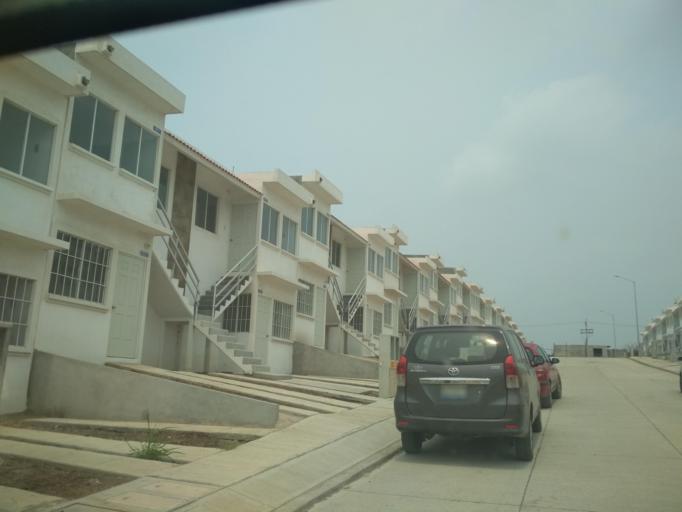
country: MX
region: Veracruz
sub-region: Veracruz
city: Rio Medio [Granja]
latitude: 19.2104
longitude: -96.2121
